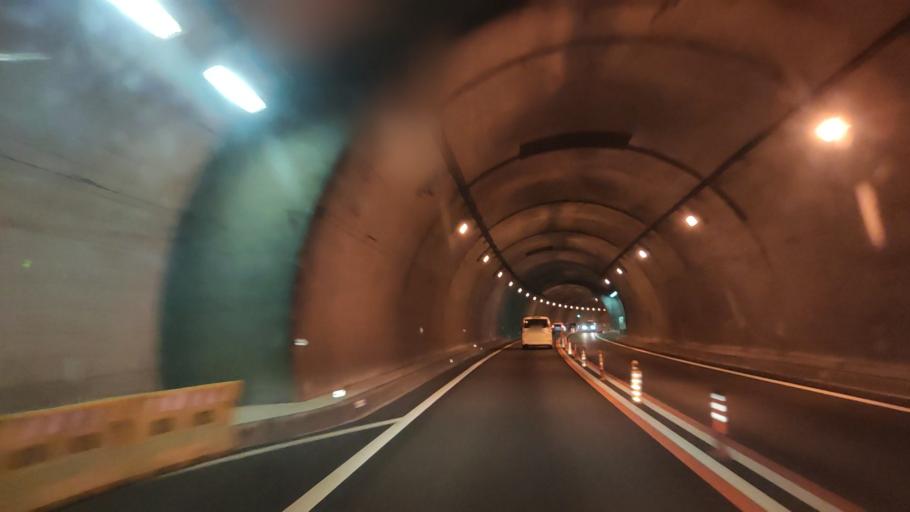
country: JP
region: Ehime
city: Kawanoecho
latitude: 33.9970
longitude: 133.6392
